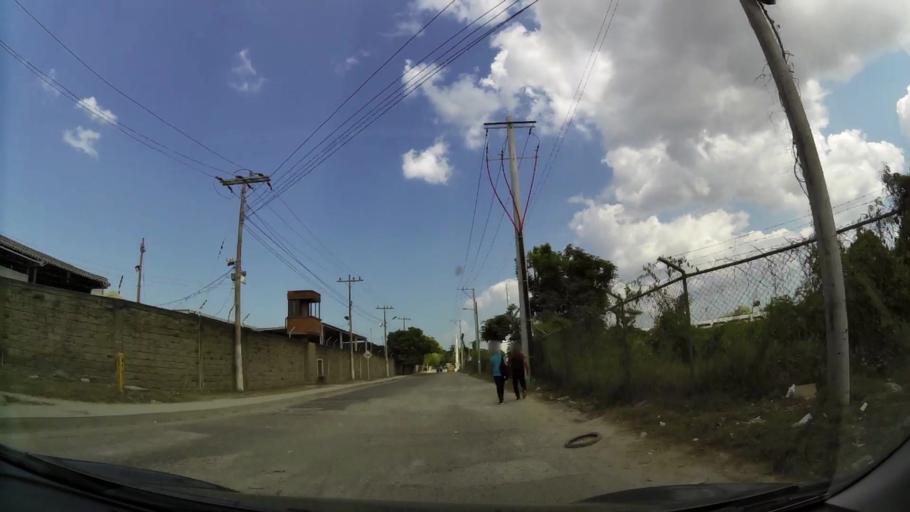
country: CO
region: Bolivar
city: Cartagena
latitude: 10.3747
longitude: -75.4629
